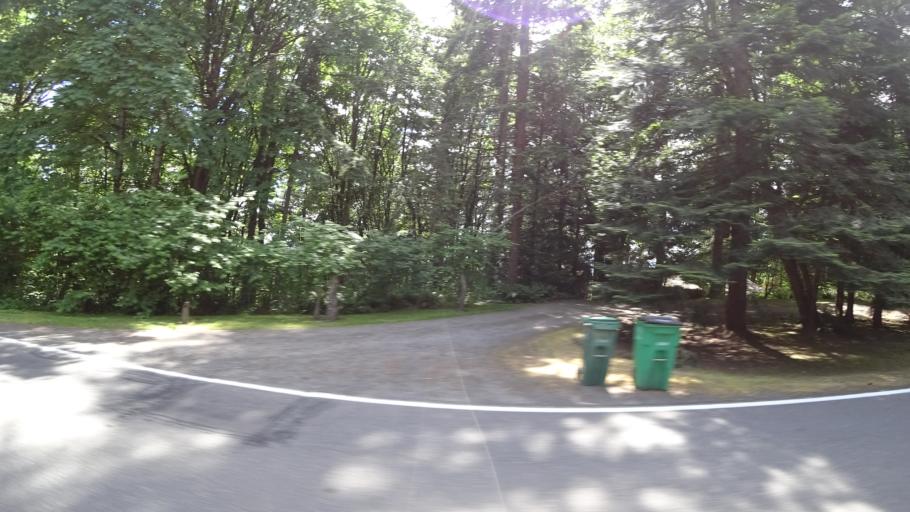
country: US
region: Oregon
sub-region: Washington County
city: Oak Hills
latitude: 45.5858
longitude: -122.8045
